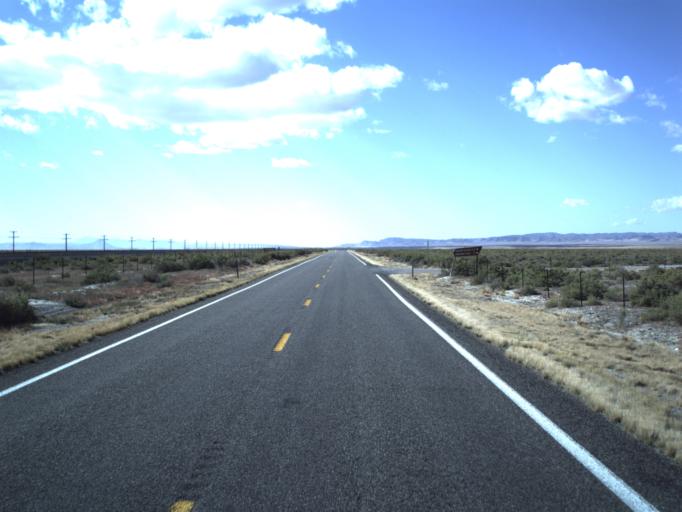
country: US
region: Utah
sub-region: Millard County
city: Delta
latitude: 39.1124
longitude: -112.7428
